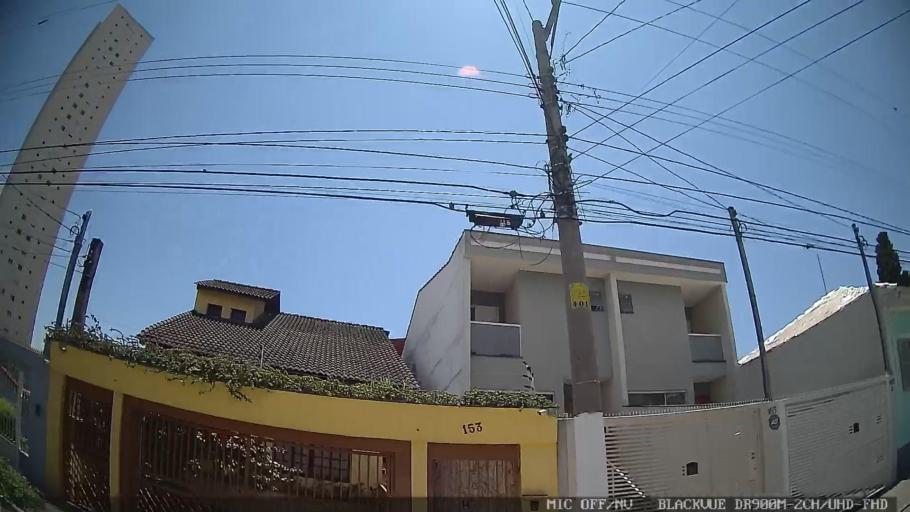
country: BR
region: Sao Paulo
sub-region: Sao Caetano Do Sul
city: Sao Caetano do Sul
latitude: -23.5643
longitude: -46.5735
